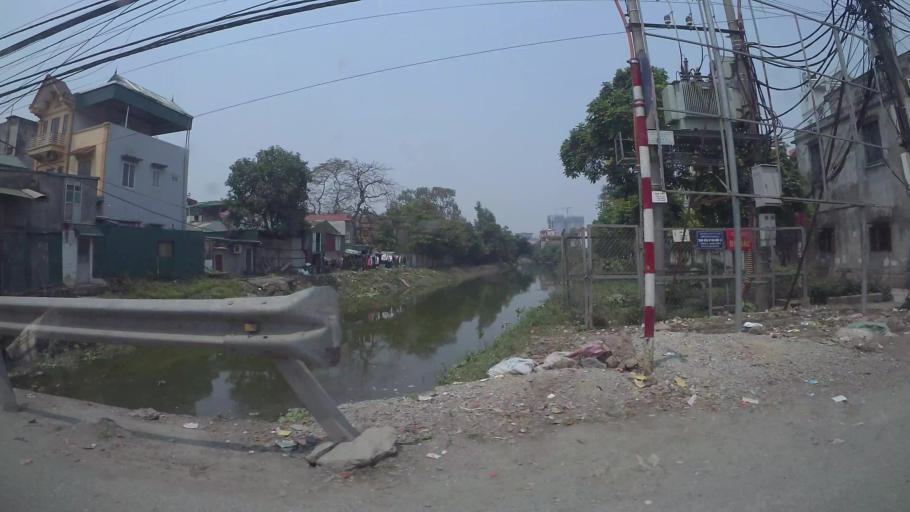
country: VN
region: Ha Noi
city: Van Dien
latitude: 20.9433
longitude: 105.8425
